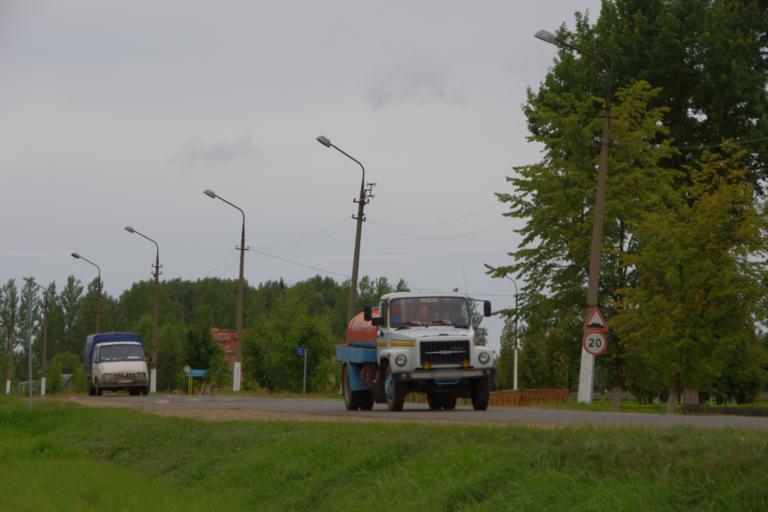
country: BY
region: Vitebsk
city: Chashniki
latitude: 55.3512
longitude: 29.2966
